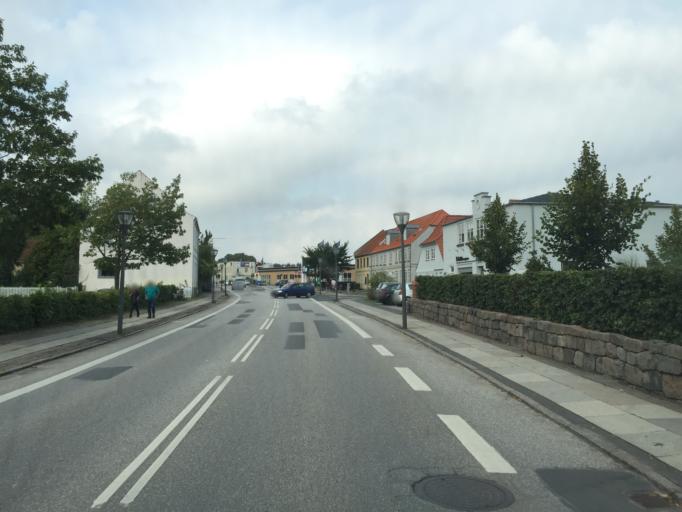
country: DK
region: South Denmark
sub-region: Nyborg Kommune
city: Nyborg
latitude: 55.3153
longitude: 10.7911
